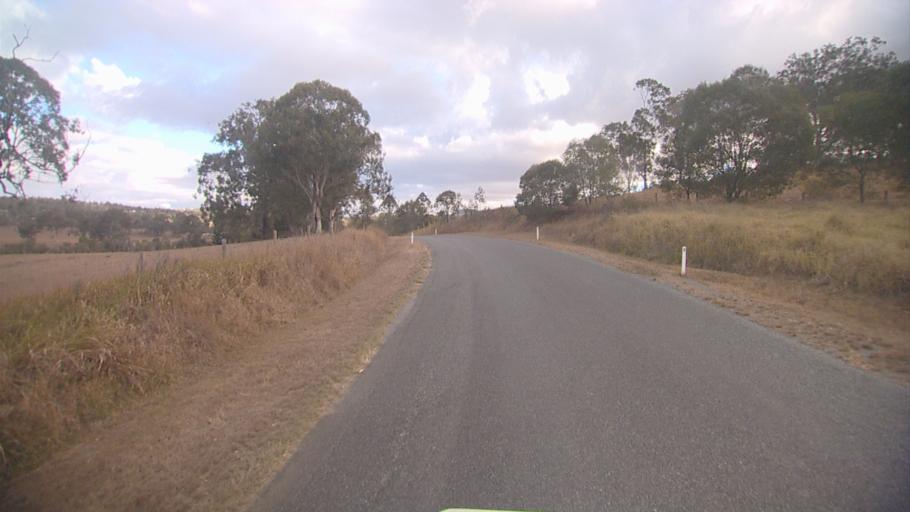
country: AU
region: Queensland
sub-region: Logan
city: Cedar Vale
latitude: -27.8910
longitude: 153.0662
